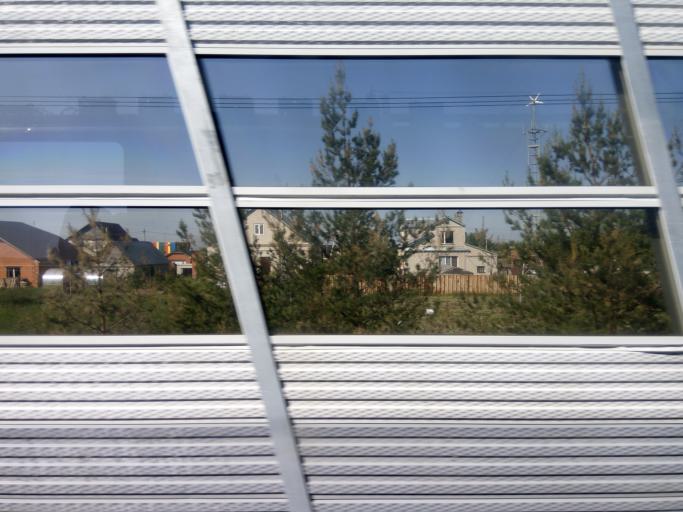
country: RU
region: Tatarstan
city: Stolbishchi
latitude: 55.6631
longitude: 49.2211
